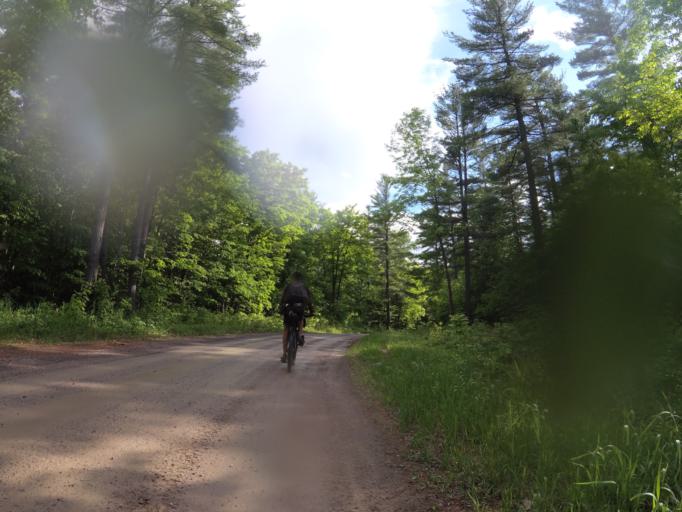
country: CA
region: Ontario
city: Renfrew
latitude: 45.1783
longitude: -76.9230
